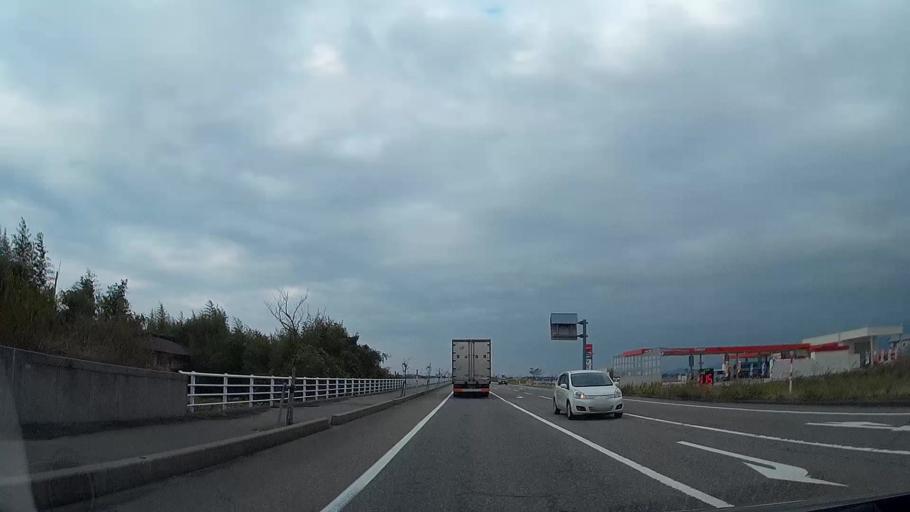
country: JP
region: Toyama
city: Nyuzen
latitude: 36.9127
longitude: 137.4582
